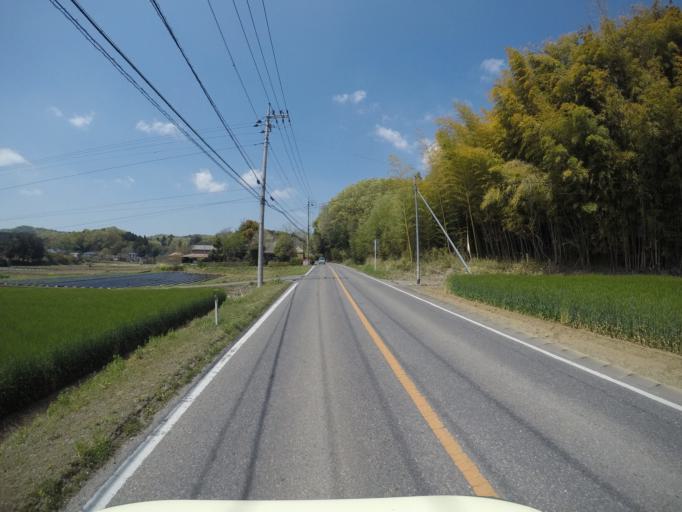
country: JP
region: Tochigi
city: Tochigi
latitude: 36.4453
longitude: 139.7136
